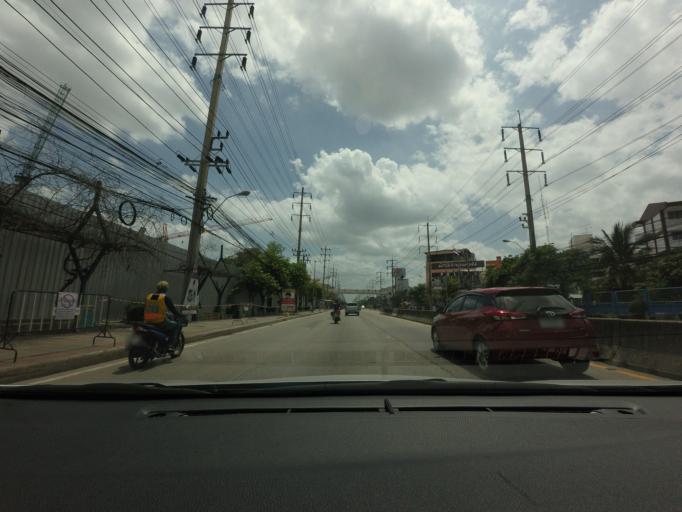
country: TH
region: Samut Prakan
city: Phra Pradaeng
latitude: 13.6478
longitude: 100.5701
